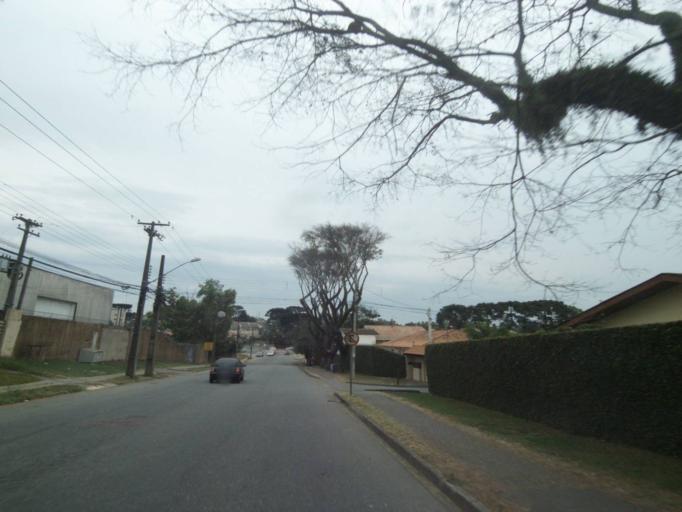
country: BR
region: Parana
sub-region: Pinhais
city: Pinhais
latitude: -25.4833
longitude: -49.2219
